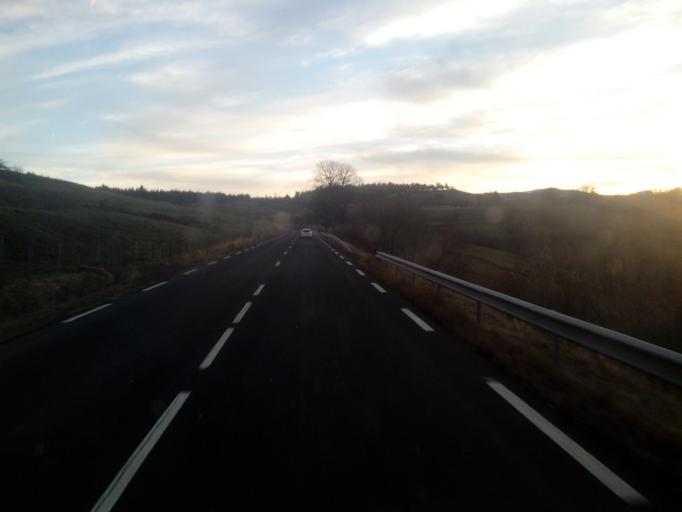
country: FR
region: Auvergne
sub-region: Departement du Cantal
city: Murat
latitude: 45.1571
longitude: 2.8253
